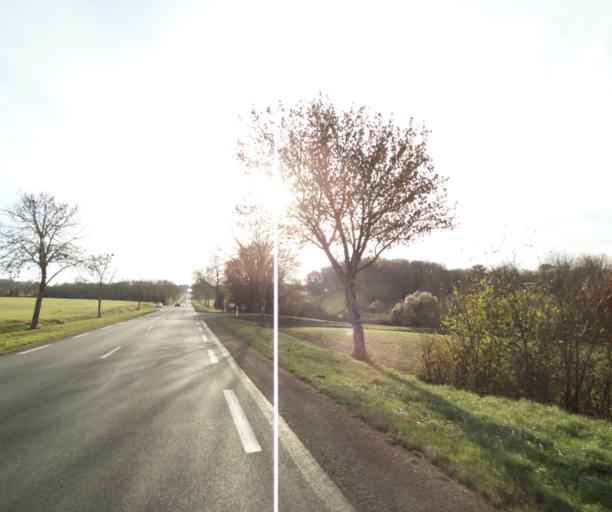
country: FR
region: Poitou-Charentes
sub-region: Departement de la Charente-Maritime
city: Saint-Hilaire-de-Villefranche
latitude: 45.8285
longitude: -0.5411
